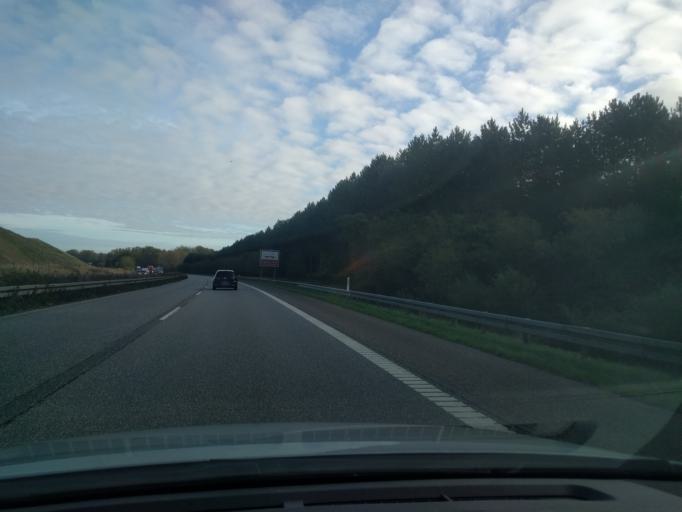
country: DK
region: Zealand
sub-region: Slagelse Kommune
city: Slagelse
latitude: 55.4056
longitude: 11.3986
